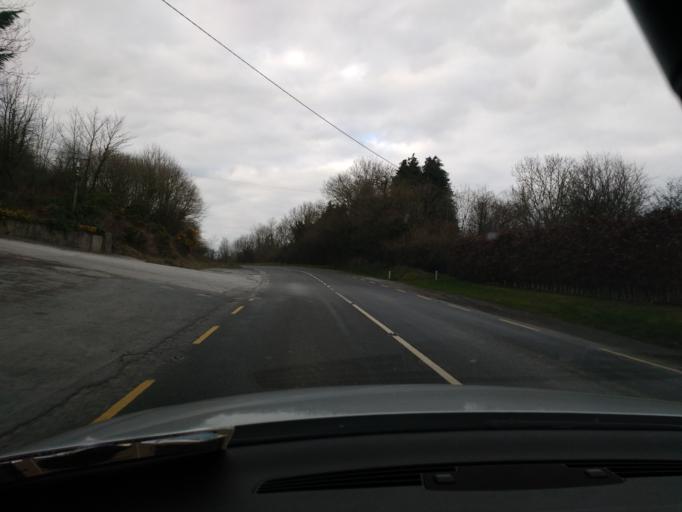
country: IE
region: Leinster
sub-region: Kilkenny
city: Kilkenny
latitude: 52.6899
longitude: -7.2763
